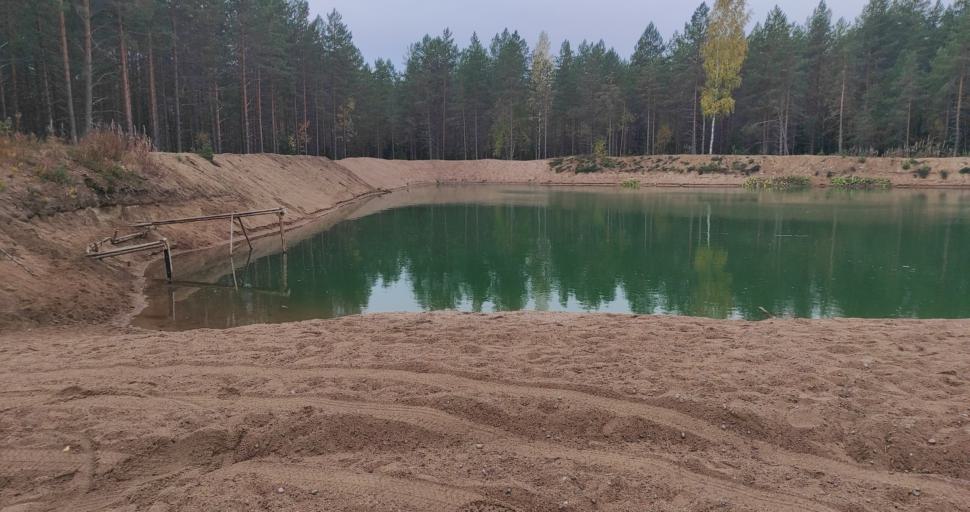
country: RU
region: Leningrad
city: Sosnovyy Bor
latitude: 60.2159
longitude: 29.1079
